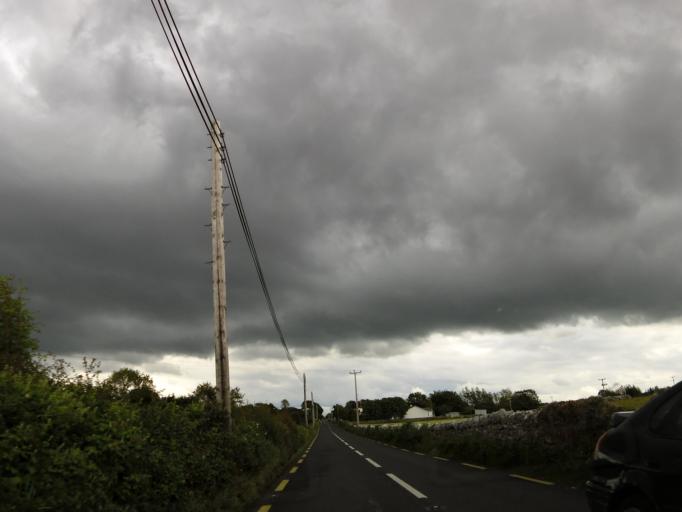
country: IE
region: Connaught
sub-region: County Galway
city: Oranmore
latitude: 53.1401
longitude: -8.9612
